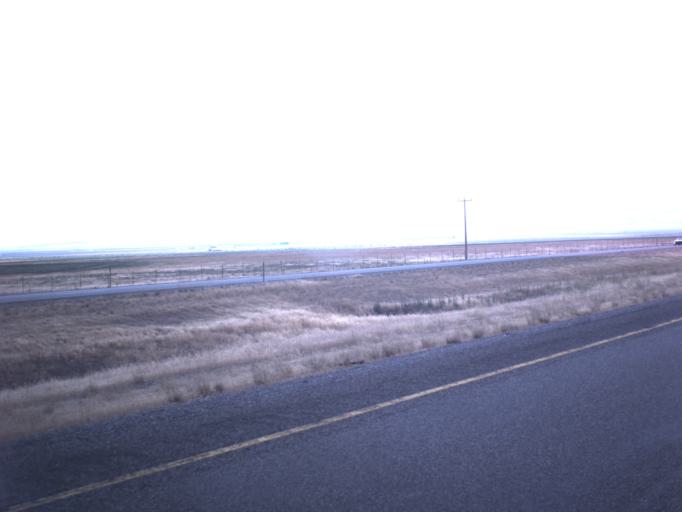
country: US
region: Idaho
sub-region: Oneida County
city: Malad City
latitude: 41.9832
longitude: -112.8070
